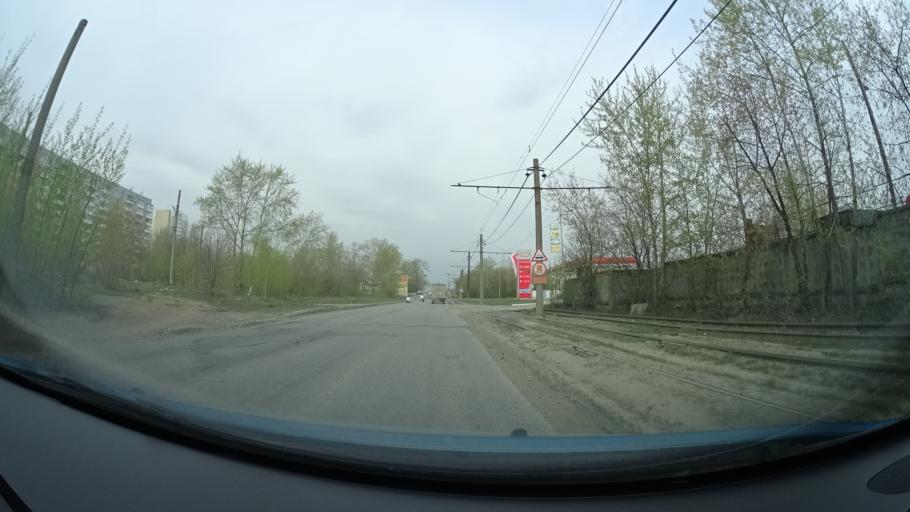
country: RU
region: Perm
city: Kondratovo
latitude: 58.0008
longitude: 56.1395
